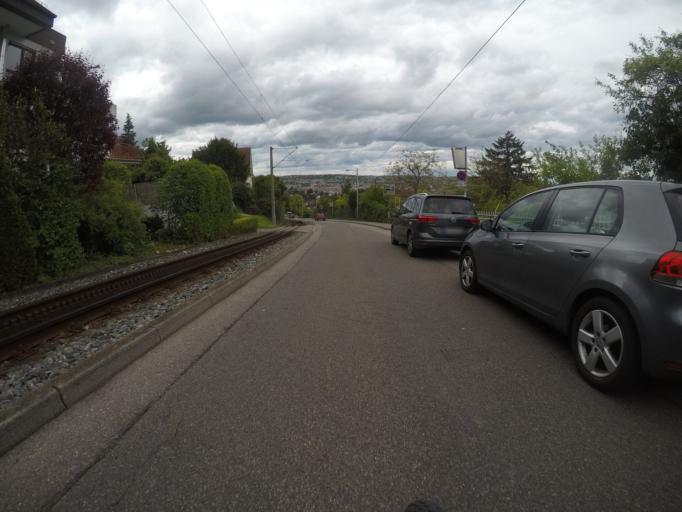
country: DE
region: Baden-Wuerttemberg
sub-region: Regierungsbezirk Stuttgart
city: Stuttgart
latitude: 48.7559
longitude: 9.1722
